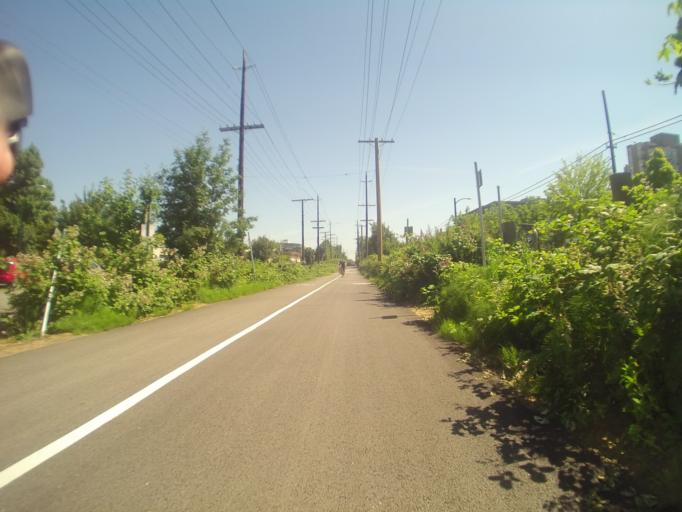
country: CA
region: British Columbia
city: Vancouver
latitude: 49.2363
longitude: -123.1553
